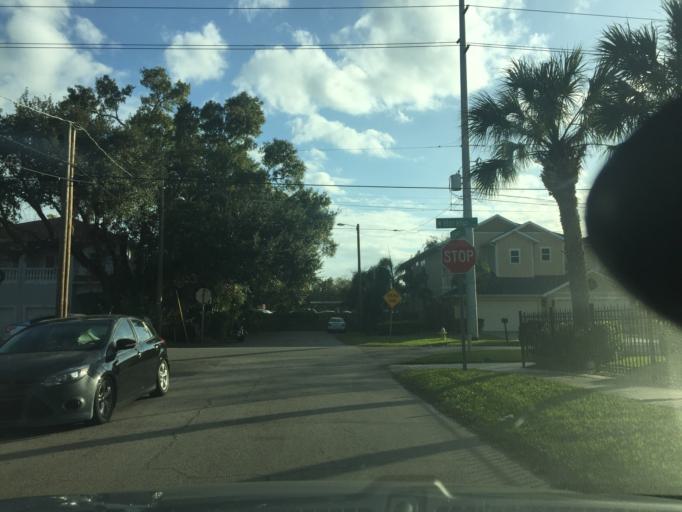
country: US
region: Florida
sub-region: Hillsborough County
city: Tampa
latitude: 27.9401
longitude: -82.4882
